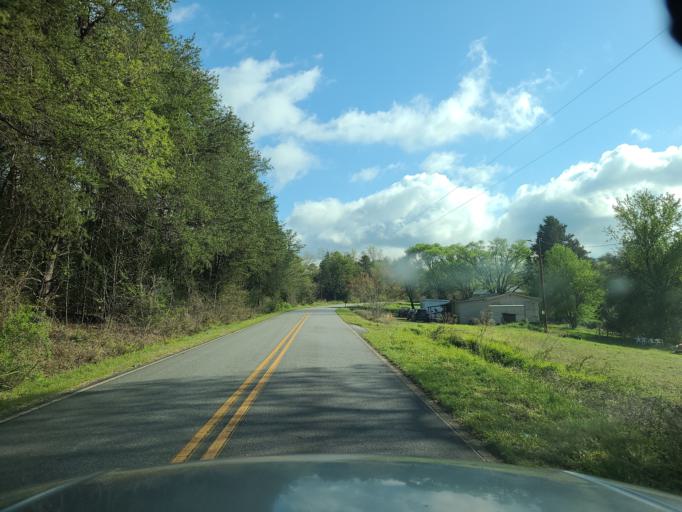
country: US
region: North Carolina
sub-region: Rutherford County
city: Forest City
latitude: 35.4121
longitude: -81.8195
